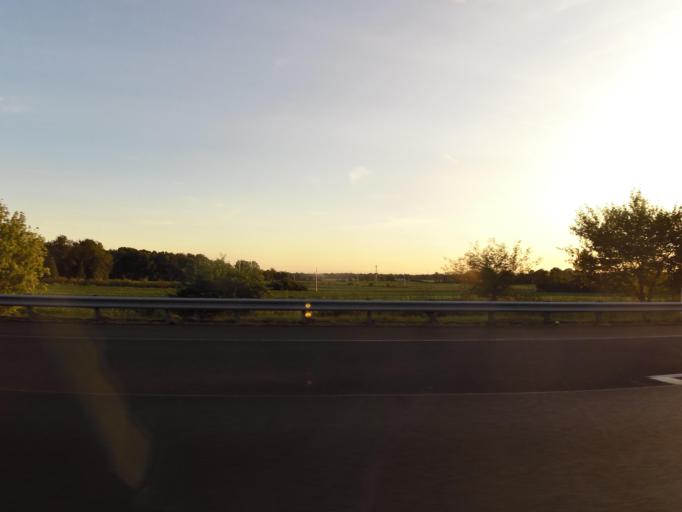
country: US
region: Indiana
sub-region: Hancock County
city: New Palestine
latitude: 39.6602
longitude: -85.9402
